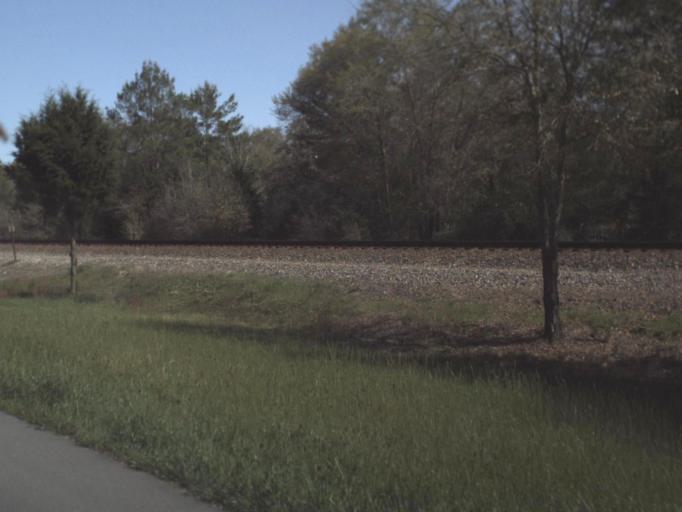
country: US
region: Florida
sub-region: Walton County
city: DeFuniak Springs
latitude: 30.7269
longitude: -86.0908
